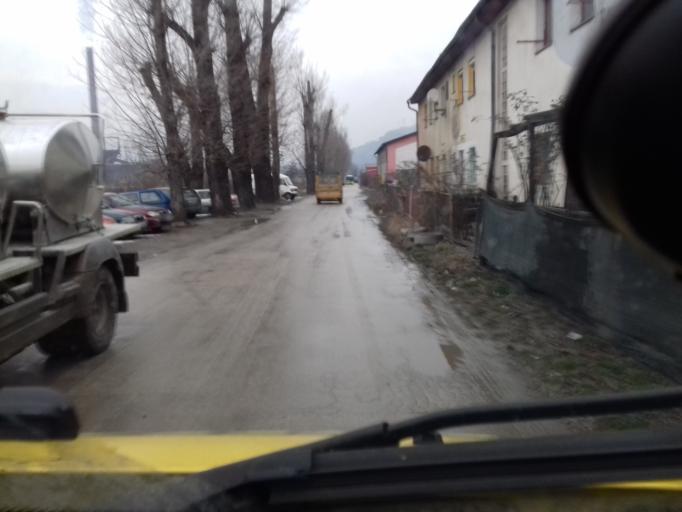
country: BA
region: Federation of Bosnia and Herzegovina
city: Zenica
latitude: 44.2196
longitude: 17.9099
